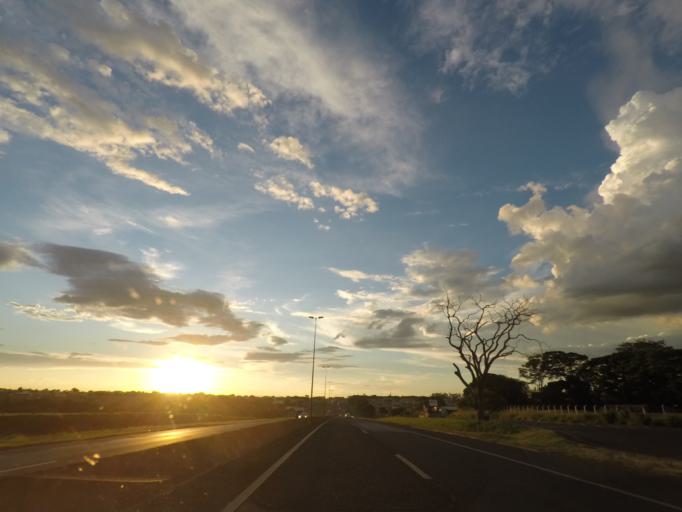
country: BR
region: Minas Gerais
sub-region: Uberaba
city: Uberaba
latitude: -19.7792
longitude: -47.9585
